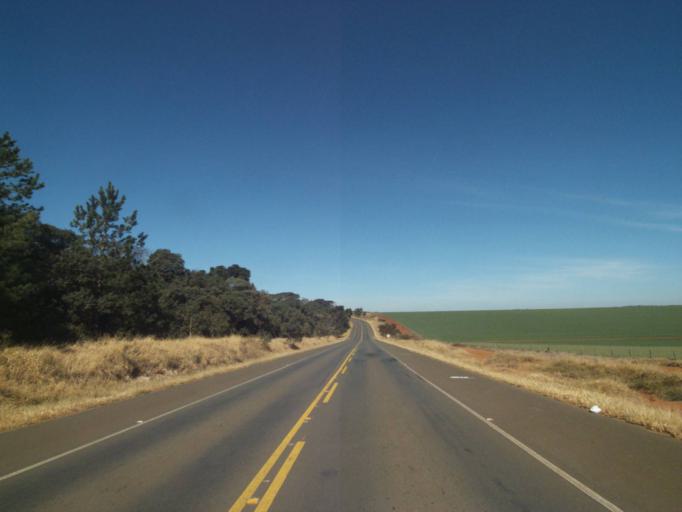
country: BR
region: Parana
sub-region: Tibagi
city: Tibagi
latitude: -24.7050
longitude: -50.4487
